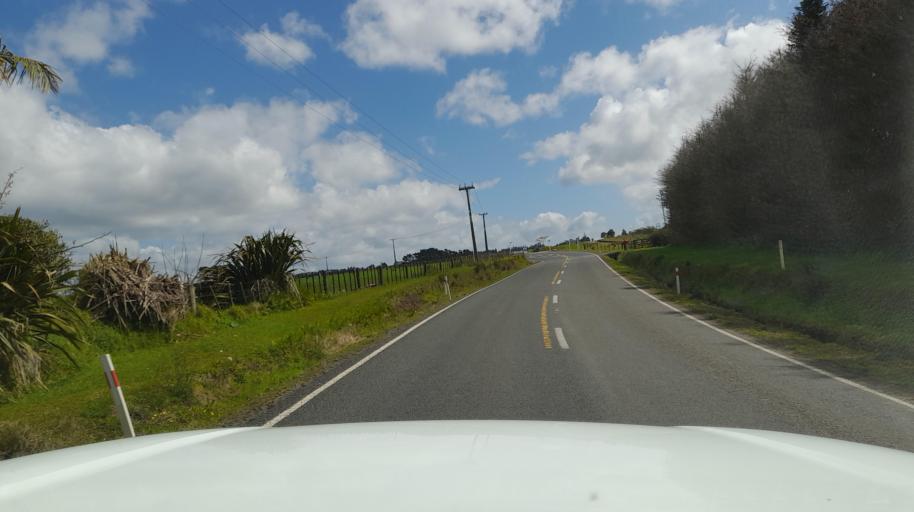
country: NZ
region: Northland
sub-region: Far North District
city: Waimate North
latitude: -35.2656
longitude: 173.8782
